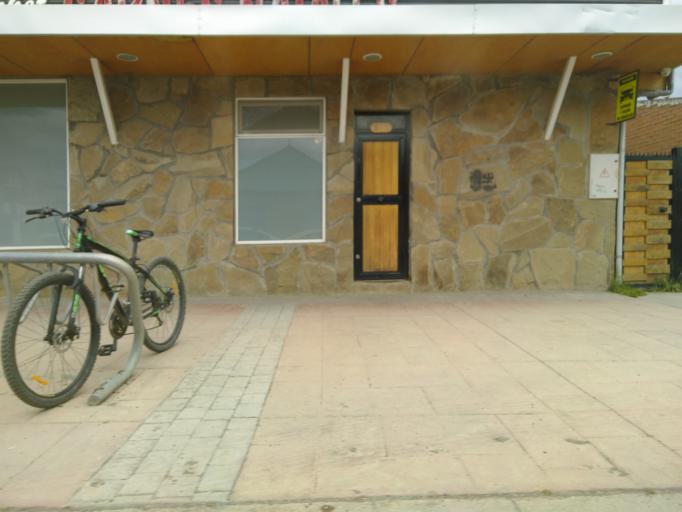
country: CL
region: Magallanes
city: Puerto Natales
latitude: -51.7294
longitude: -72.5025
